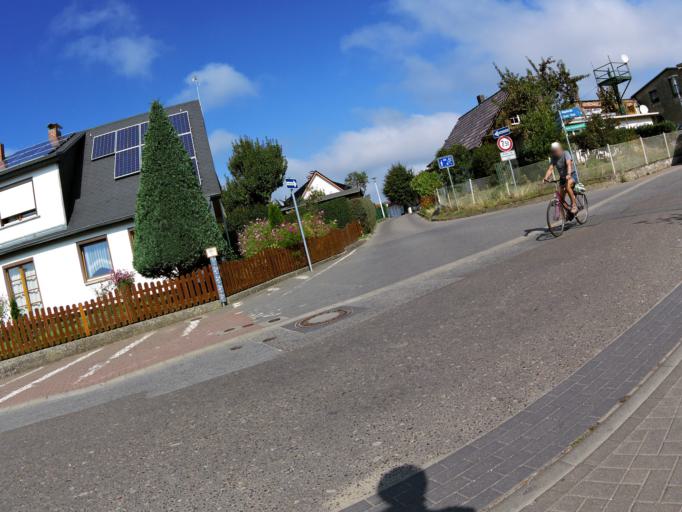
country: DE
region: Mecklenburg-Vorpommern
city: Loddin
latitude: 54.0119
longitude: 14.0428
